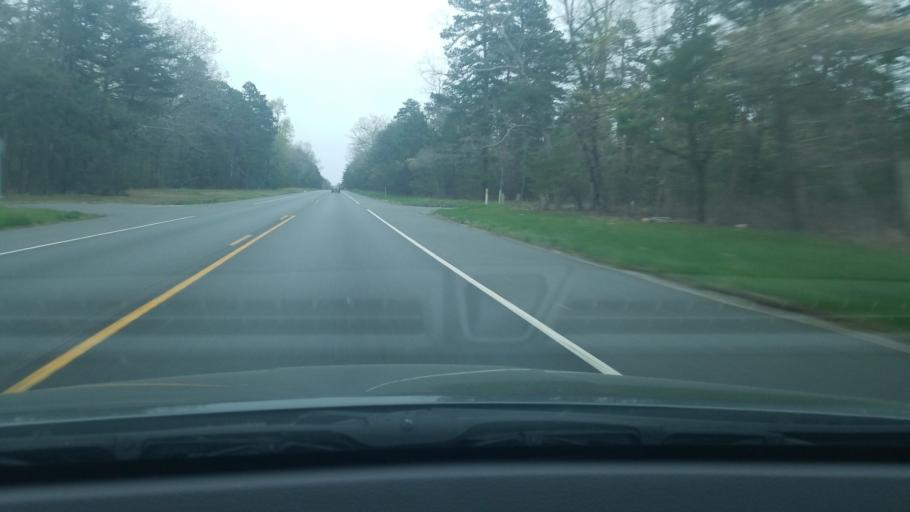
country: US
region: New Jersey
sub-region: Burlington County
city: Magnolia
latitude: 39.8905
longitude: -74.6361
